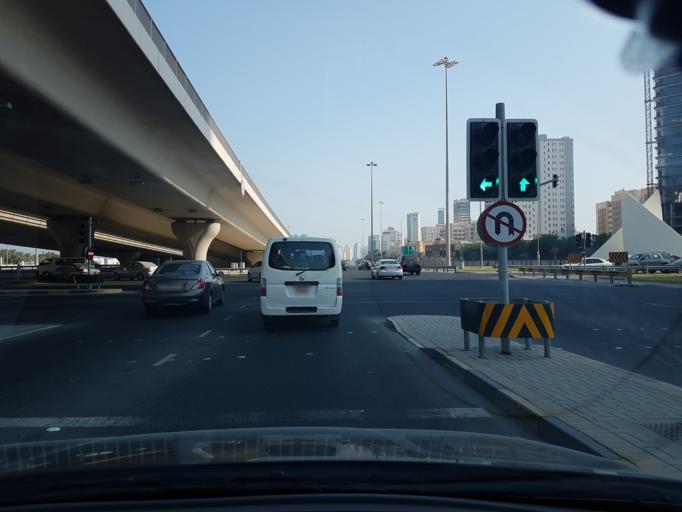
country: BH
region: Muharraq
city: Al Muharraq
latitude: 26.2422
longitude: 50.5937
